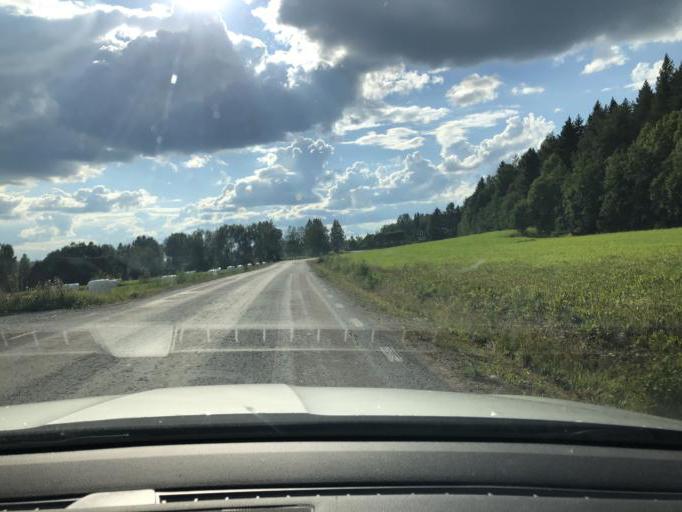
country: SE
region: Vaesternorrland
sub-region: Solleftea Kommun
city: Solleftea
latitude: 63.1989
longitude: 17.0959
